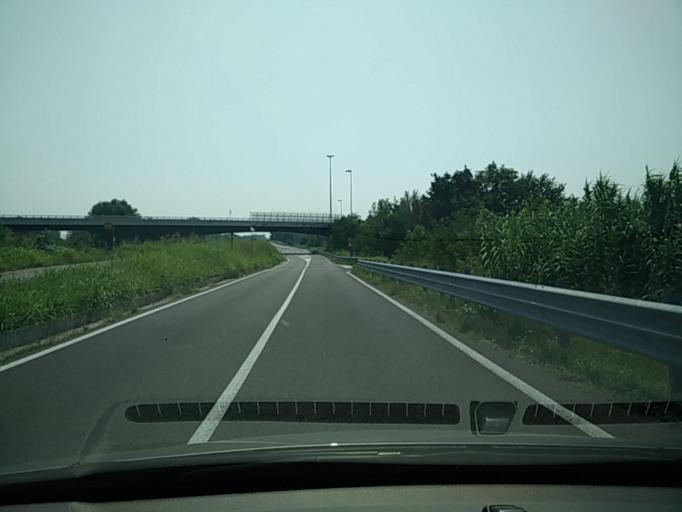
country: IT
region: Veneto
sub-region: Provincia di Venezia
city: Passarella
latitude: 45.6062
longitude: 12.5937
